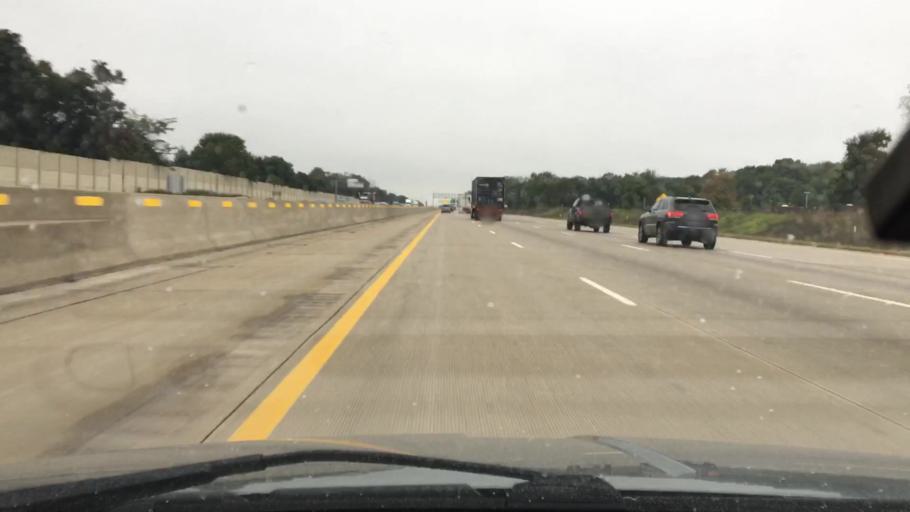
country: US
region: Michigan
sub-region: Kalamazoo County
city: Portage
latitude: 42.2379
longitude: -85.6194
